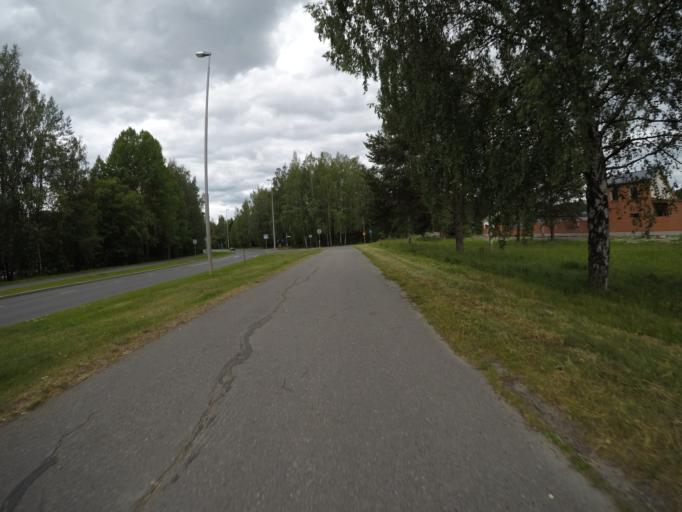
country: FI
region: Haeme
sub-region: Haemeenlinna
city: Haemeenlinna
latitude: 60.9905
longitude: 24.4347
